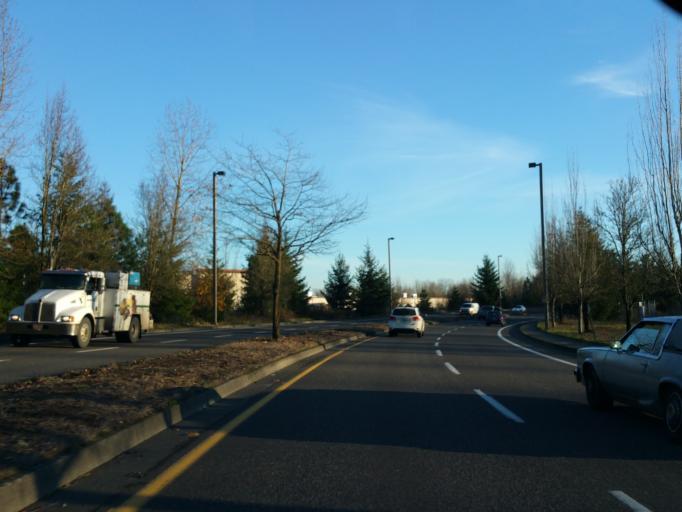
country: US
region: Oregon
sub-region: Multnomah County
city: Fairview
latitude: 45.5528
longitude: -122.4789
